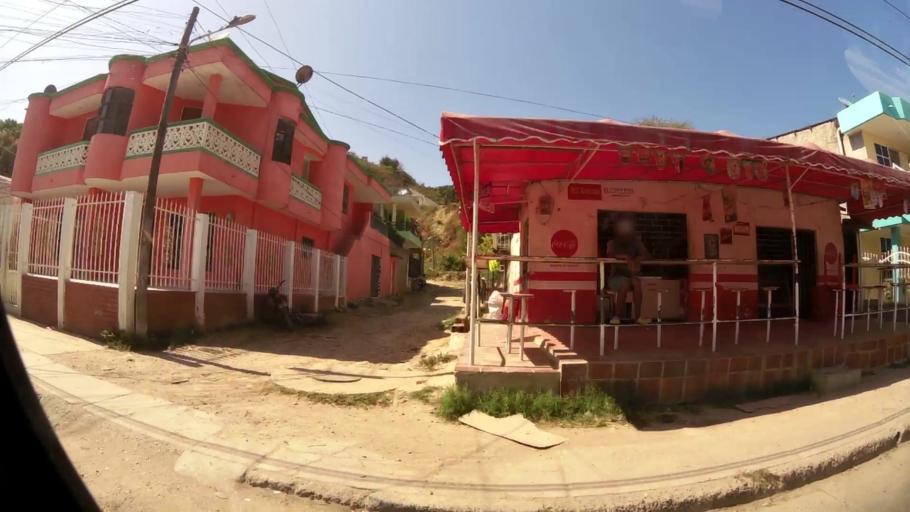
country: CO
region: Bolivar
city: Cartagena
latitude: 10.4246
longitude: -75.5165
